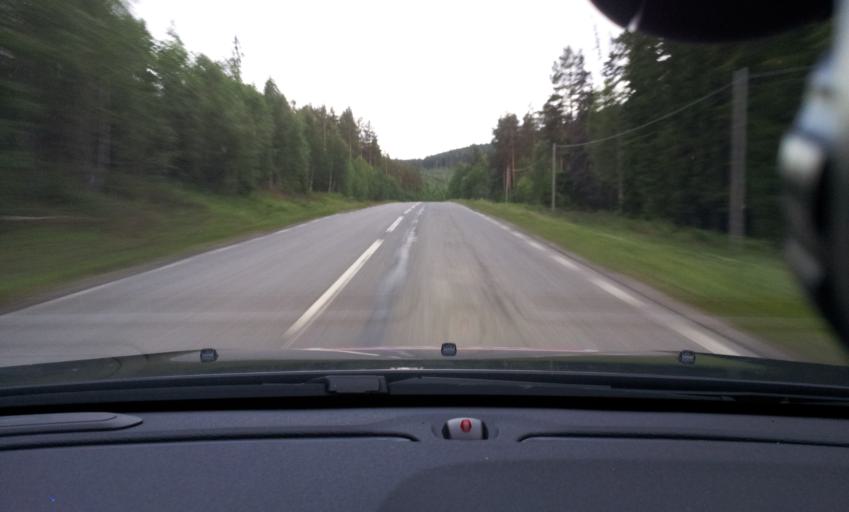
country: SE
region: Jaemtland
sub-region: Ragunda Kommun
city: Hammarstrand
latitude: 63.0566
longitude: 16.3899
